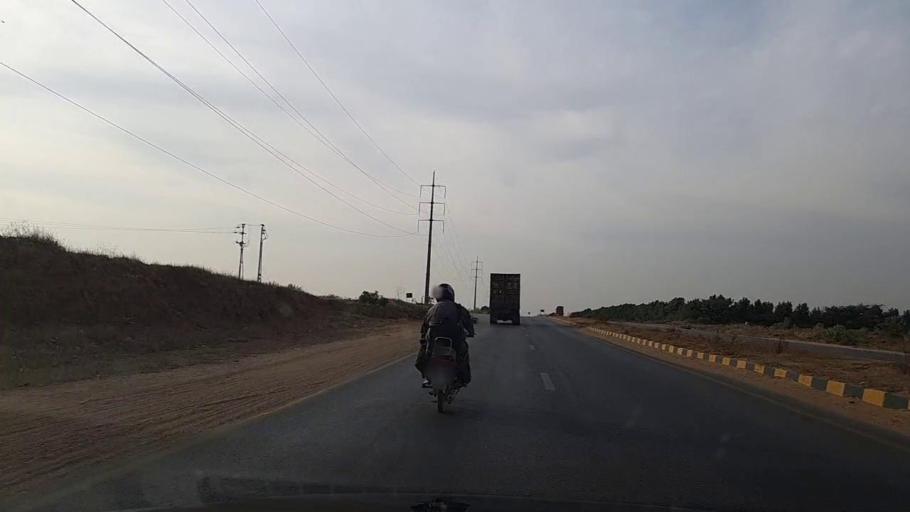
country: PK
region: Sindh
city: Gharo
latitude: 24.8198
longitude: 67.4850
